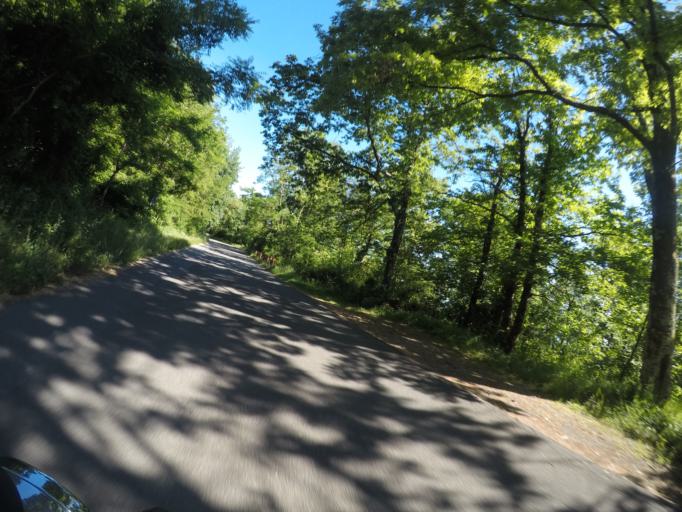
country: IT
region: Tuscany
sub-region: Provincia di Massa-Carrara
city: Fosdinovo
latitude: 44.1161
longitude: 10.0639
